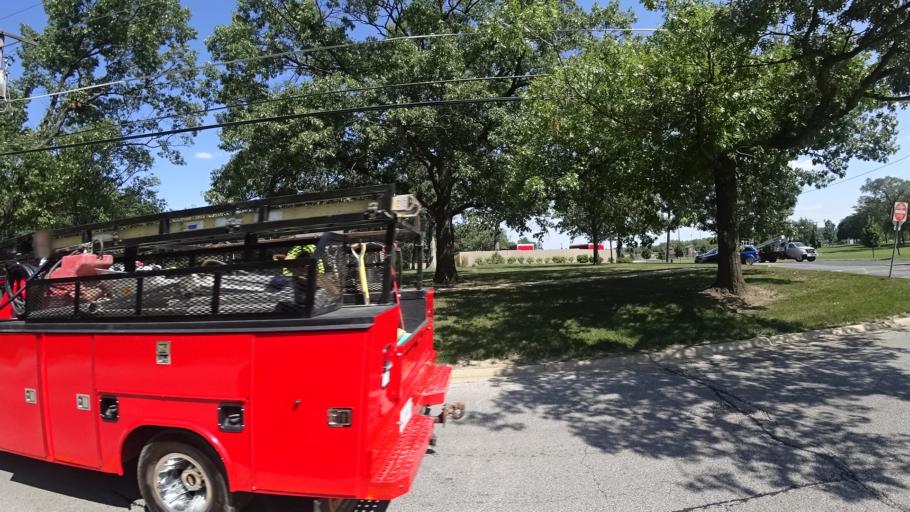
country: US
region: Illinois
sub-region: Cook County
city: Orland Park
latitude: 41.6231
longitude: -87.8633
